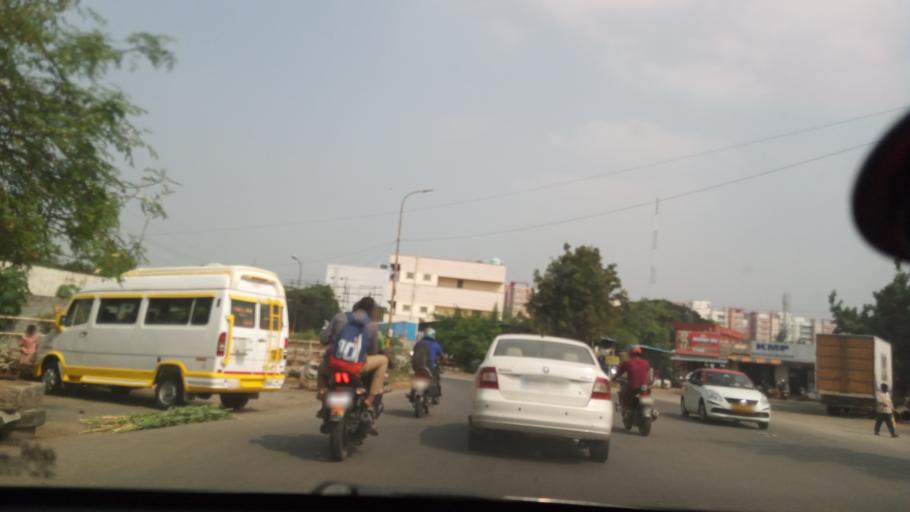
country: IN
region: Tamil Nadu
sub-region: Coimbatore
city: Coimbatore
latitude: 11.0210
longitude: 76.9861
